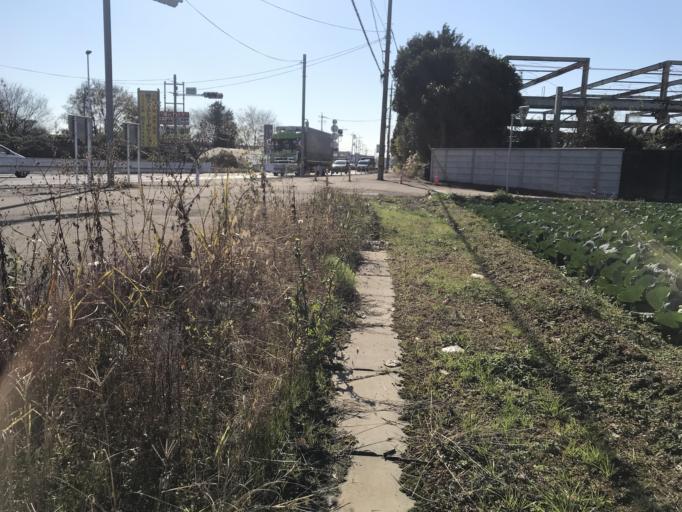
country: JP
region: Ibaraki
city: Sakai
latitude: 36.1340
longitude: 139.8052
